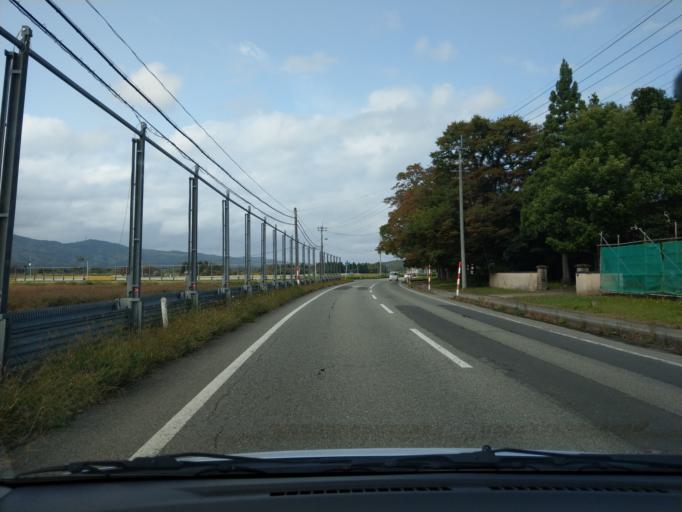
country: JP
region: Akita
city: Omagari
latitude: 39.5290
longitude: 140.2609
